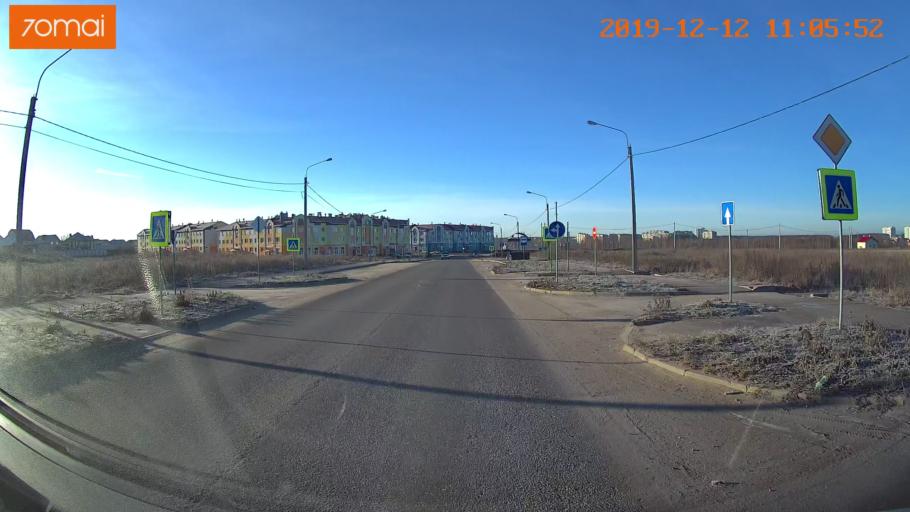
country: RU
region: Ivanovo
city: Kokhma
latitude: 56.9466
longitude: 41.0927
